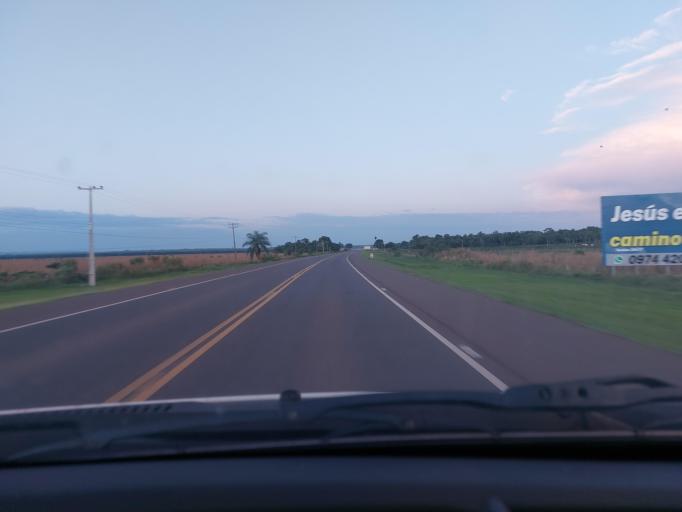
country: PY
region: San Pedro
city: Union
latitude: -24.7021
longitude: -56.5083
